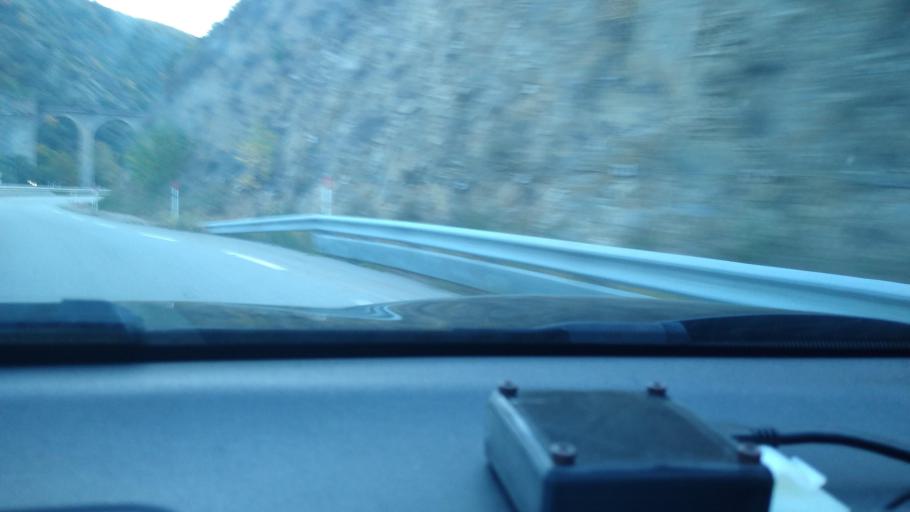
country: FR
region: Languedoc-Roussillon
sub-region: Departement des Pyrenees-Orientales
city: Vernet-les-Bains
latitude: 42.5194
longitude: 2.2038
